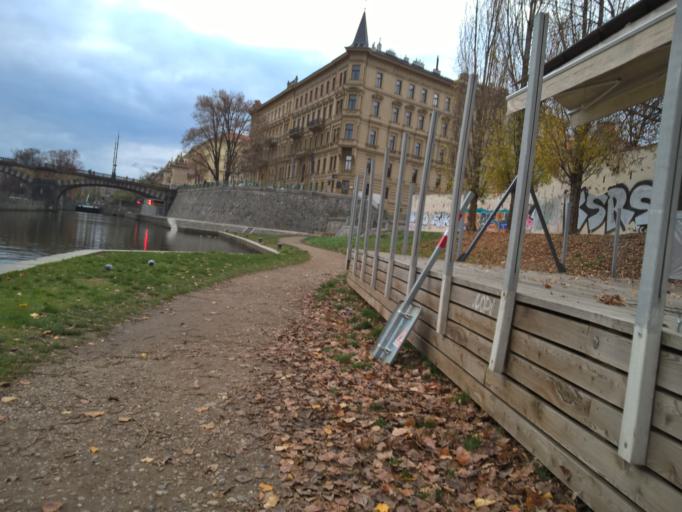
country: CZ
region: Praha
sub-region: Praha 1
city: Mala Strana
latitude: 50.0827
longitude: 14.4083
